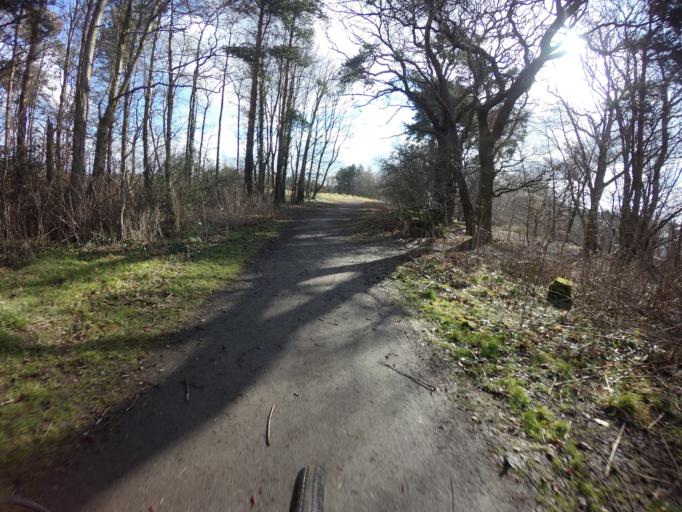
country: GB
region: Scotland
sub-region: West Lothian
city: Mid Calder
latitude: 55.8906
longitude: -3.4988
